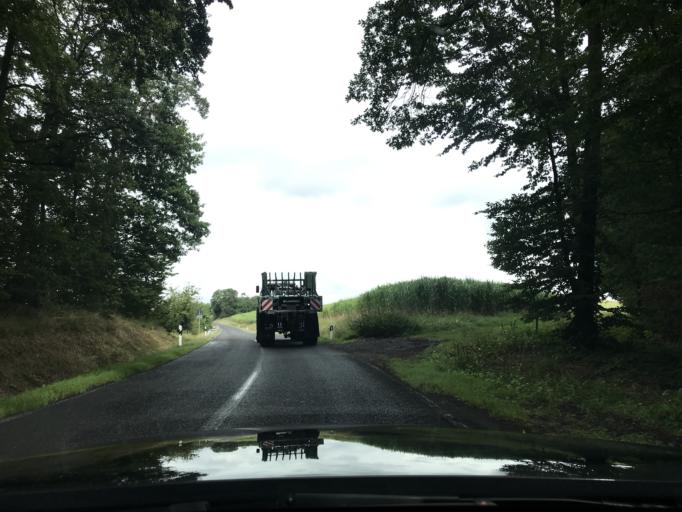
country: DE
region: Bavaria
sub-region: Regierungsbezirk Unterfranken
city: Breitbrunn
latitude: 50.0553
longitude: 10.6679
